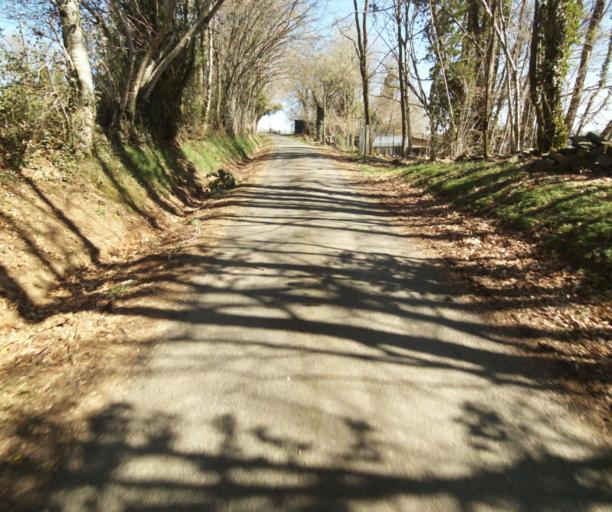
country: FR
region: Limousin
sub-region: Departement de la Correze
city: Chamboulive
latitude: 45.3955
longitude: 1.6619
